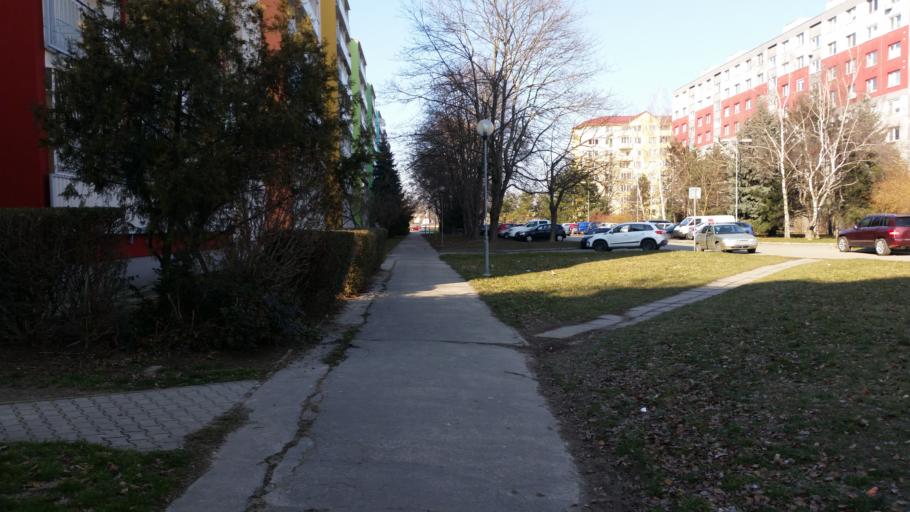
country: SK
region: Bratislavsky
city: Bratislava
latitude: 48.1627
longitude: 17.1679
